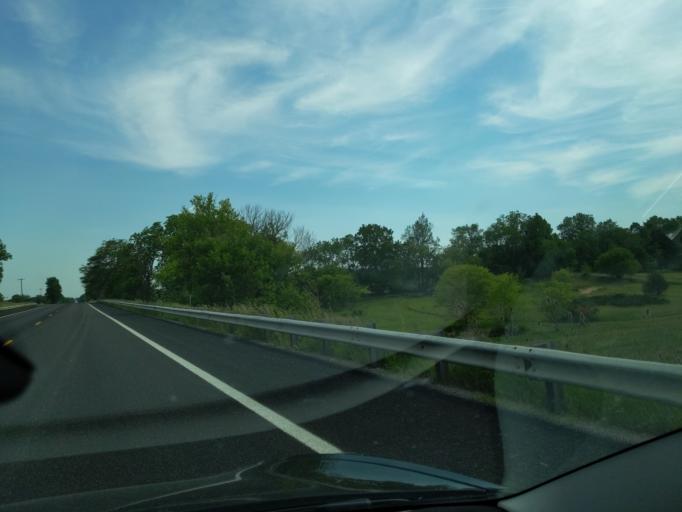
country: US
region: Michigan
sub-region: Ionia County
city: Lake Odessa
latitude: 42.7119
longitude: -85.0951
